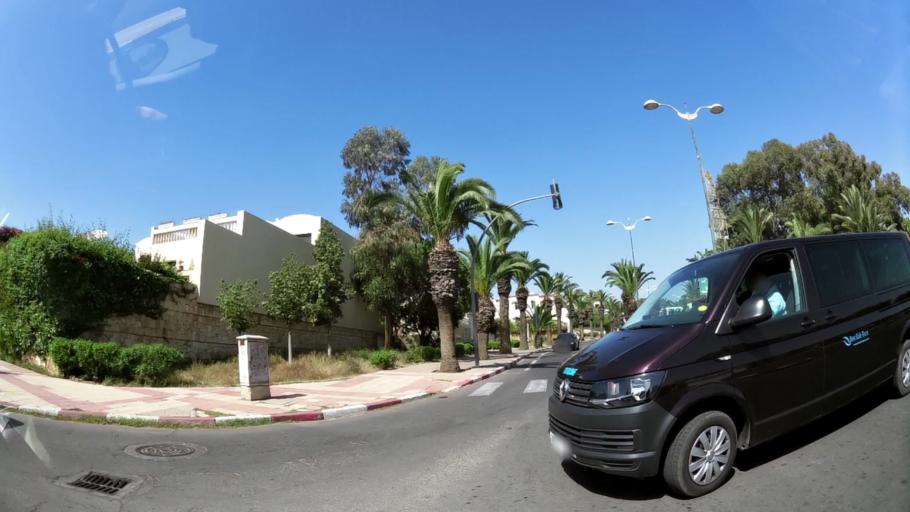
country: MA
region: Souss-Massa-Draa
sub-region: Agadir-Ida-ou-Tnan
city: Agadir
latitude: 30.4249
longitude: -9.5987
